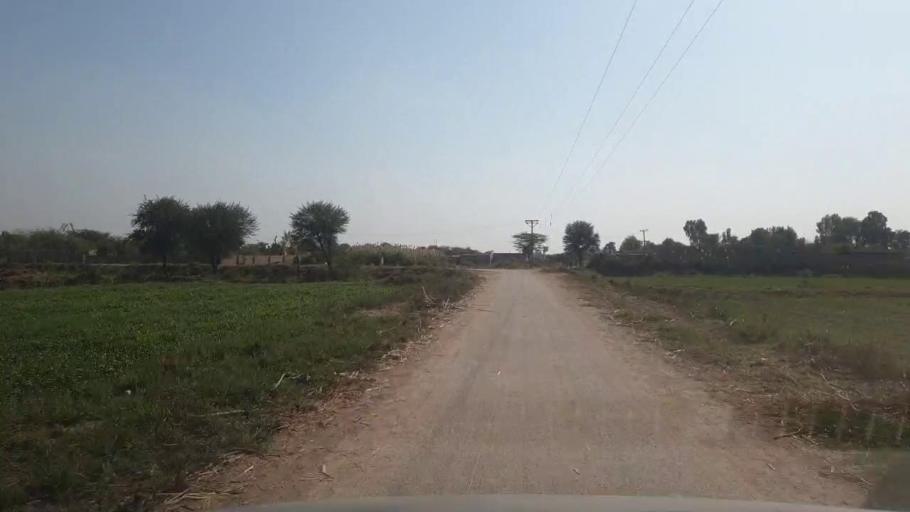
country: PK
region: Sindh
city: Chambar
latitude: 25.3208
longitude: 68.8656
